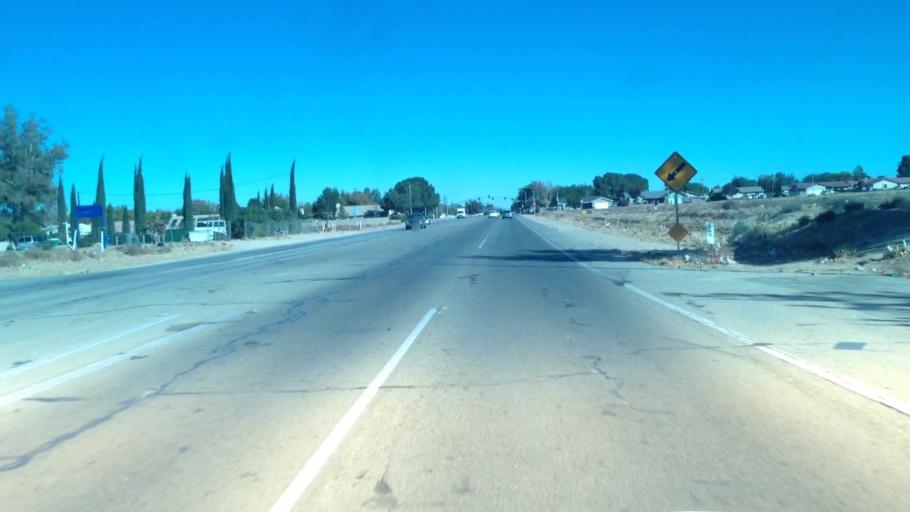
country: US
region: California
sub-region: Los Angeles County
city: Quartz Hill
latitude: 34.6603
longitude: -118.1792
